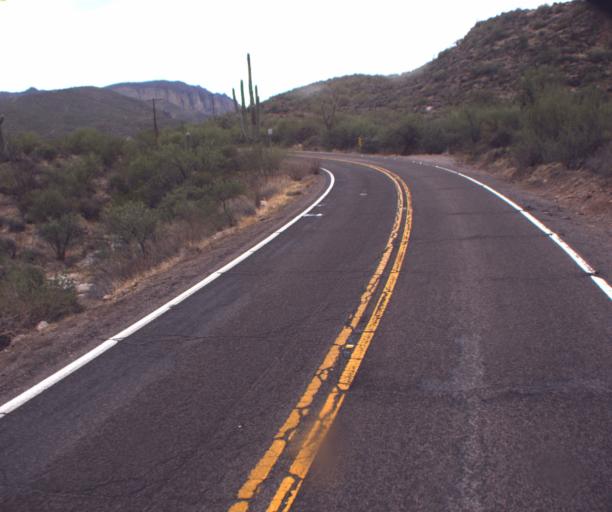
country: US
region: Arizona
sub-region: Pinal County
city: Apache Junction
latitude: 33.5349
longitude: -111.4309
